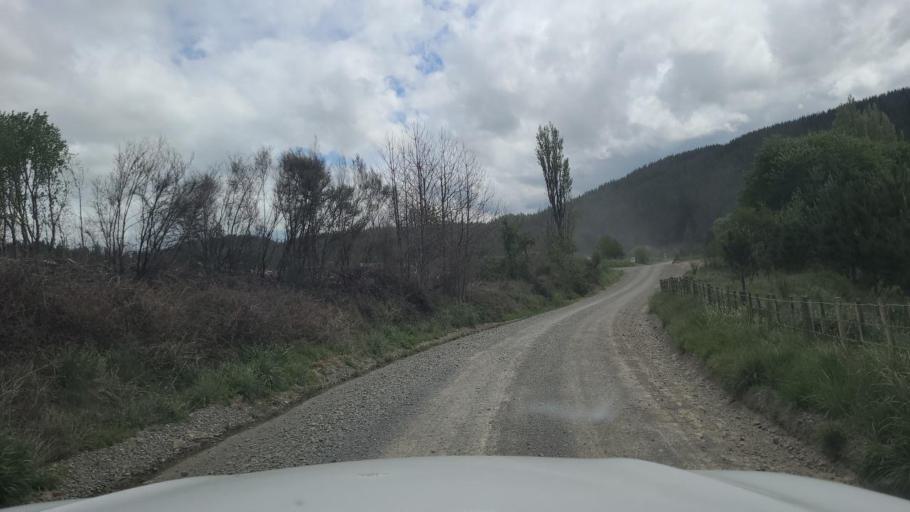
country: NZ
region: Hawke's Bay
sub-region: Napier City
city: Taradale
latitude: -39.2750
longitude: 176.6759
